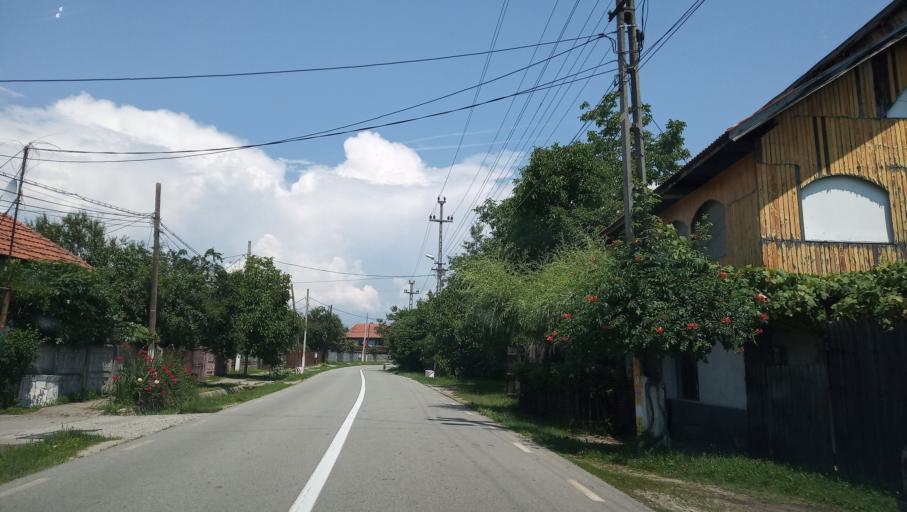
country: RO
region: Gorj
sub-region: Comuna Turcinesti
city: Turcinesti
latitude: 45.0496
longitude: 23.3465
